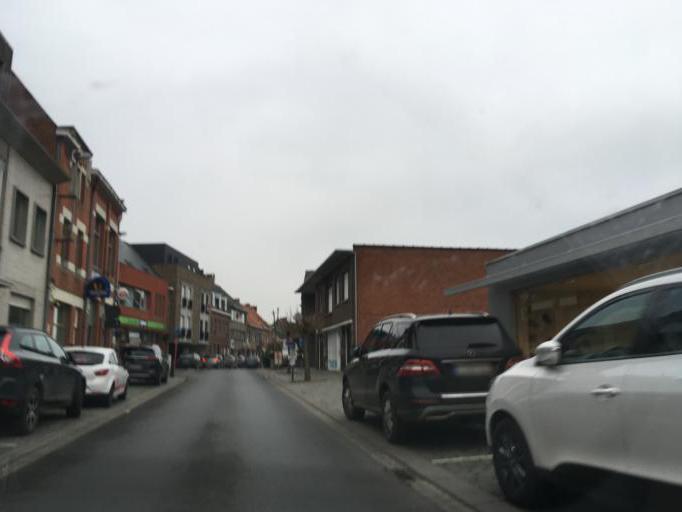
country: BE
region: Flanders
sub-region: Provincie West-Vlaanderen
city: Roeselare
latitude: 50.9339
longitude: 3.1554
